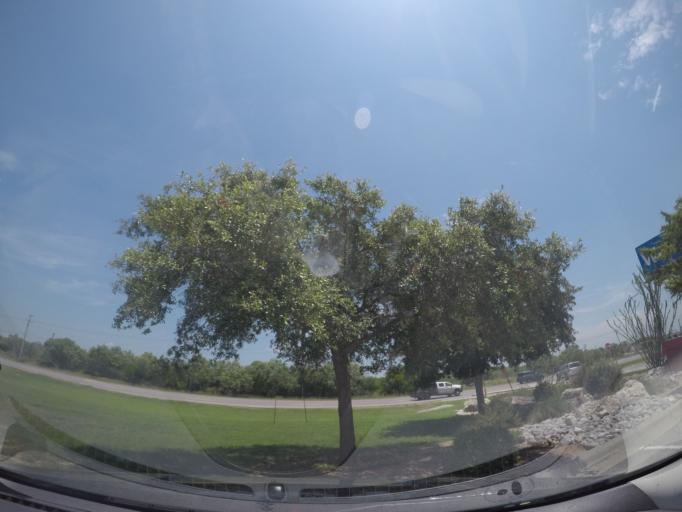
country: US
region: Texas
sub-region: Uvalde County
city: Uvalde
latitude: 29.2341
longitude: -99.7525
